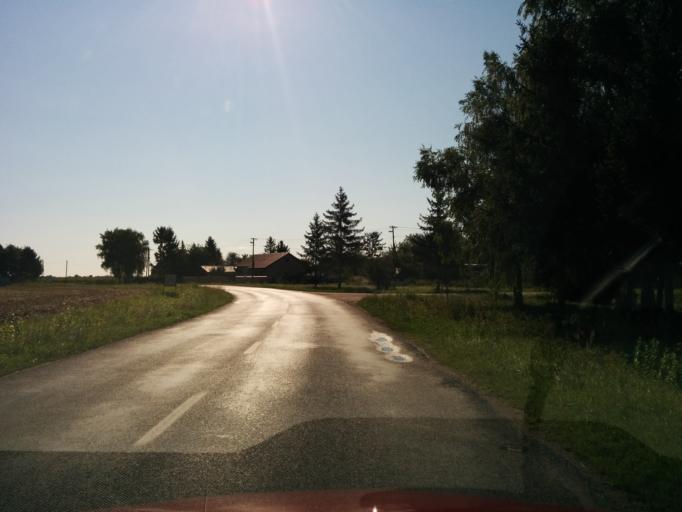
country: HU
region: Vas
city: Buk
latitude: 47.3665
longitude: 16.8217
